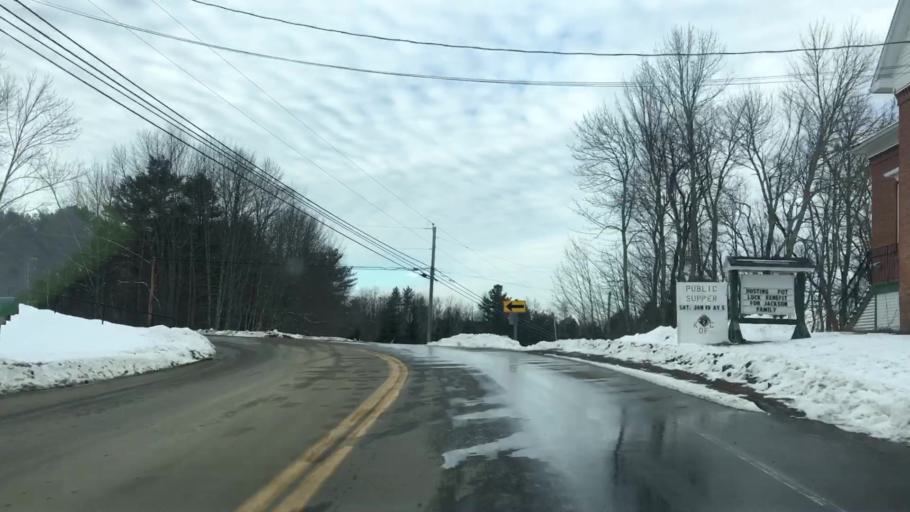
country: US
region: Maine
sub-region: Lincoln County
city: Whitefield
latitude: 44.2288
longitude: -69.6132
